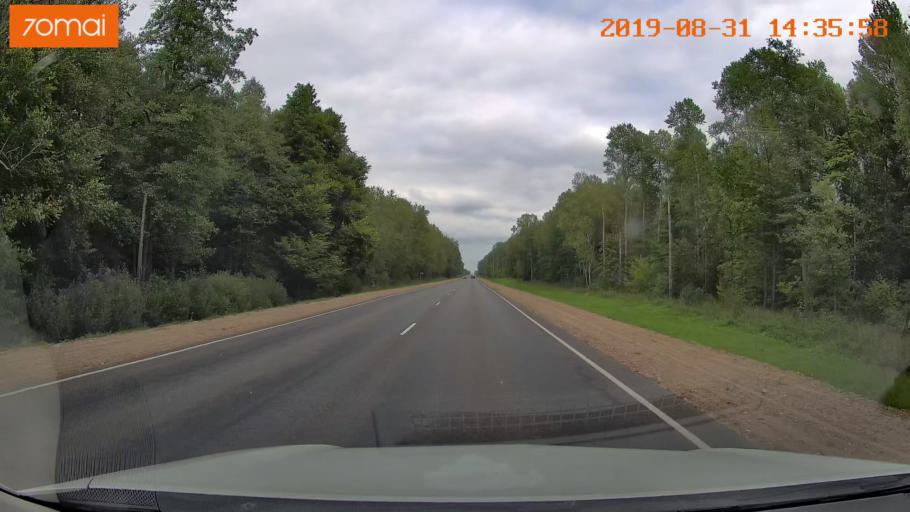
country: RU
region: Smolensk
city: Yekimovichi
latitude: 54.1665
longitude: 33.4682
